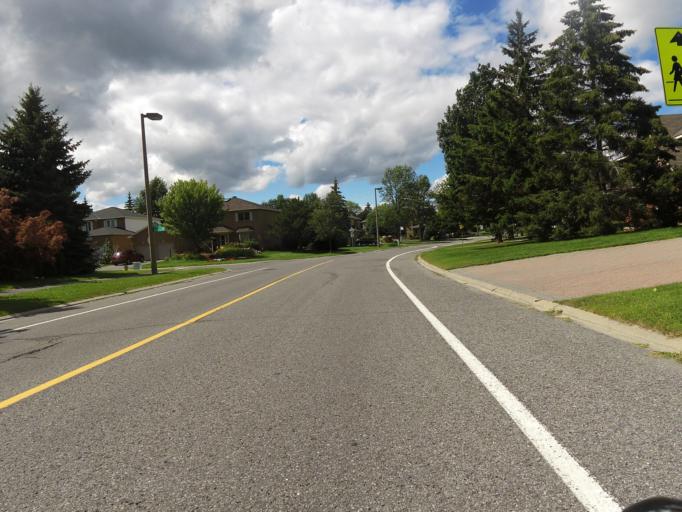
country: CA
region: Ontario
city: Bells Corners
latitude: 45.3215
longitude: -75.9065
